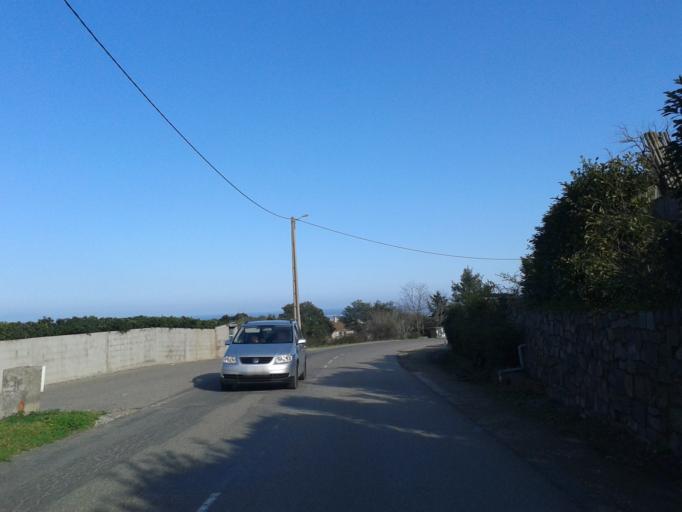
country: FR
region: Corsica
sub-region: Departement de la Haute-Corse
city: Biguglia
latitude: 42.5938
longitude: 9.4269
